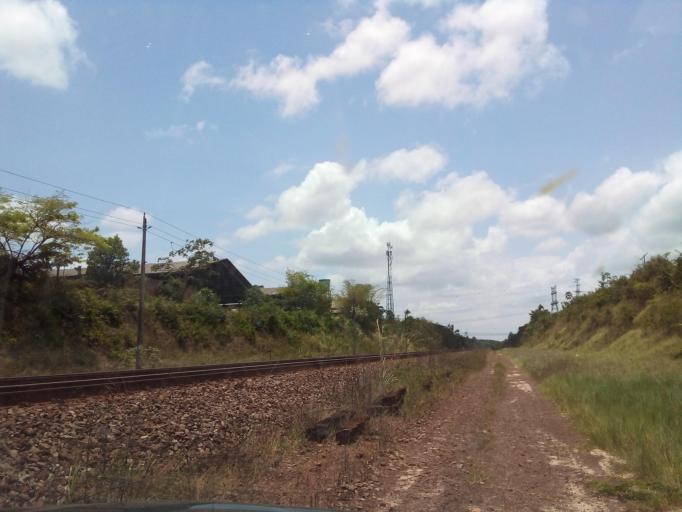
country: BR
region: Maranhao
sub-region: Sao Luis
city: Sao Luis
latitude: -2.7062
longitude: -44.3150
